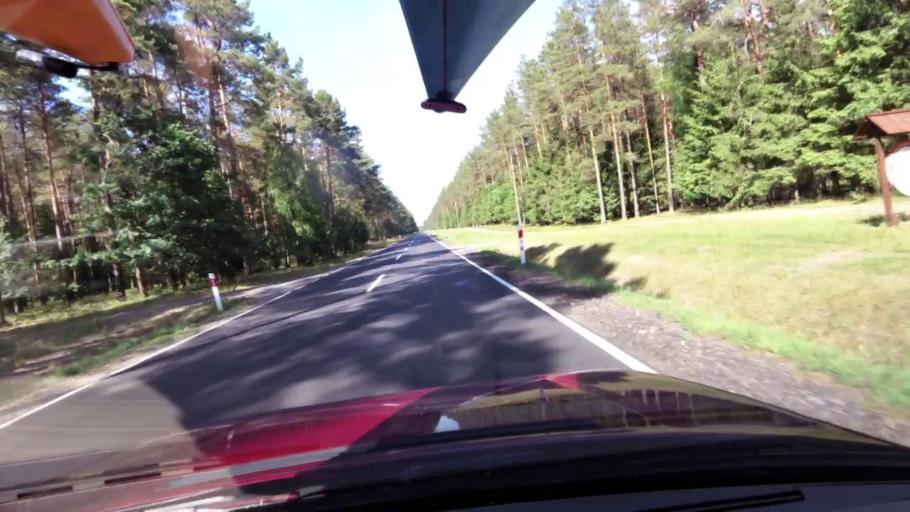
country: PL
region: Pomeranian Voivodeship
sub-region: Powiat bytowski
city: Trzebielino
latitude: 54.1339
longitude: 17.0170
